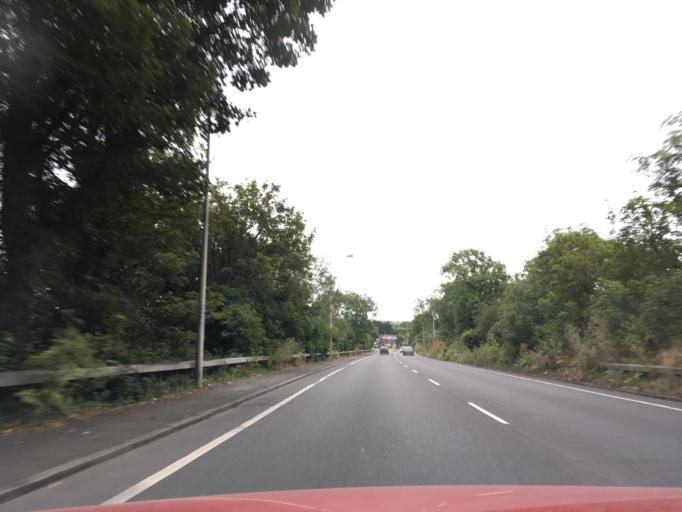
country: GB
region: England
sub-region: Central Bedfordshire
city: Houghton Regis
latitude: 51.9050
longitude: -0.5486
